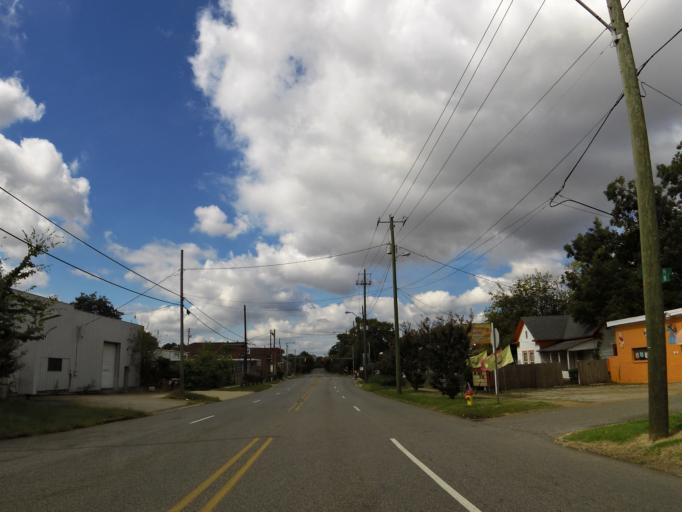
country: US
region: Alabama
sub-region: Jefferson County
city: Birmingham
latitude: 33.5032
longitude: -86.8335
